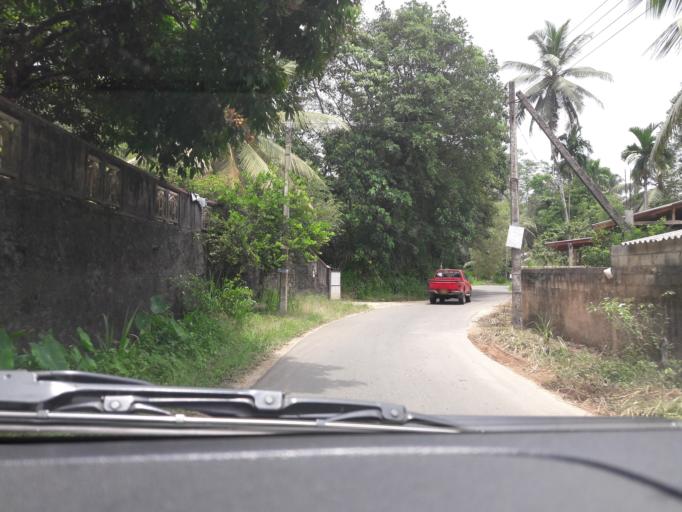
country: LK
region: Southern
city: Galle
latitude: 6.1802
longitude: 80.2908
